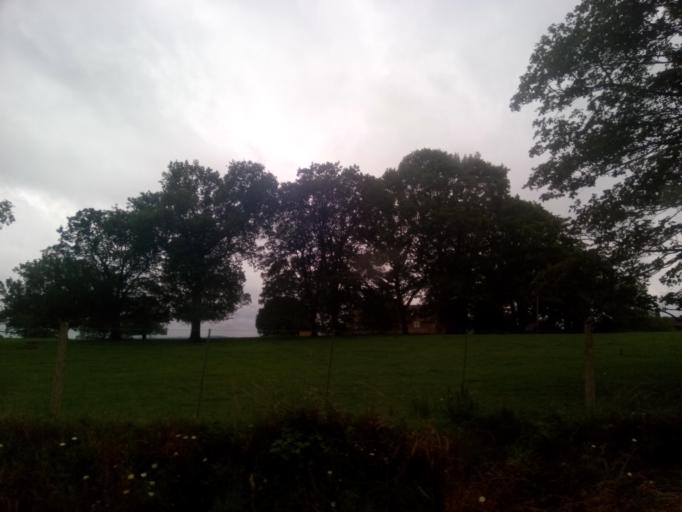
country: GB
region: England
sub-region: North Yorkshire
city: Settle
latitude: 54.0156
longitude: -2.2524
